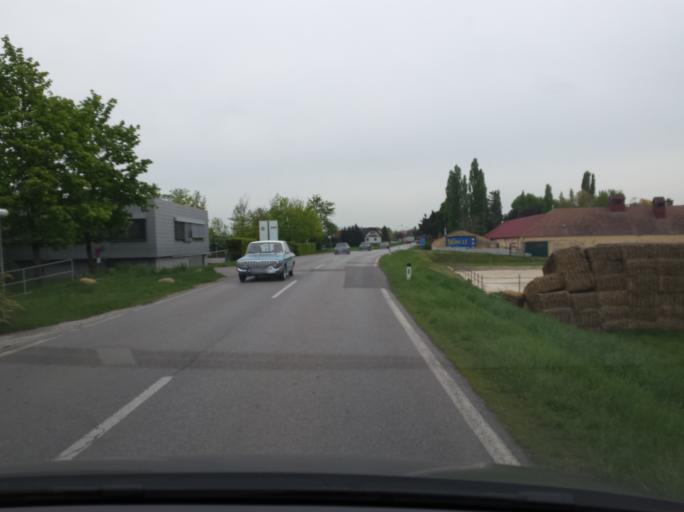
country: AT
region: Lower Austria
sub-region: Politischer Bezirk Bruck an der Leitha
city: Bruck an der Leitha
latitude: 48.0336
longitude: 16.7672
